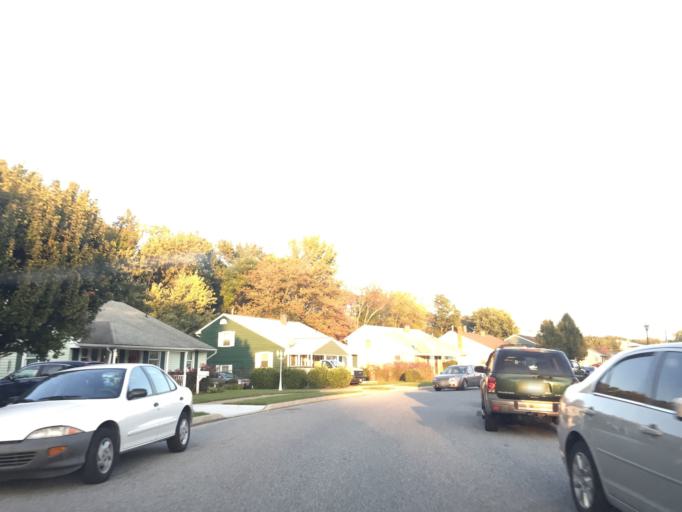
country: US
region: Maryland
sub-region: Baltimore County
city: Essex
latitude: 39.3215
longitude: -76.4754
